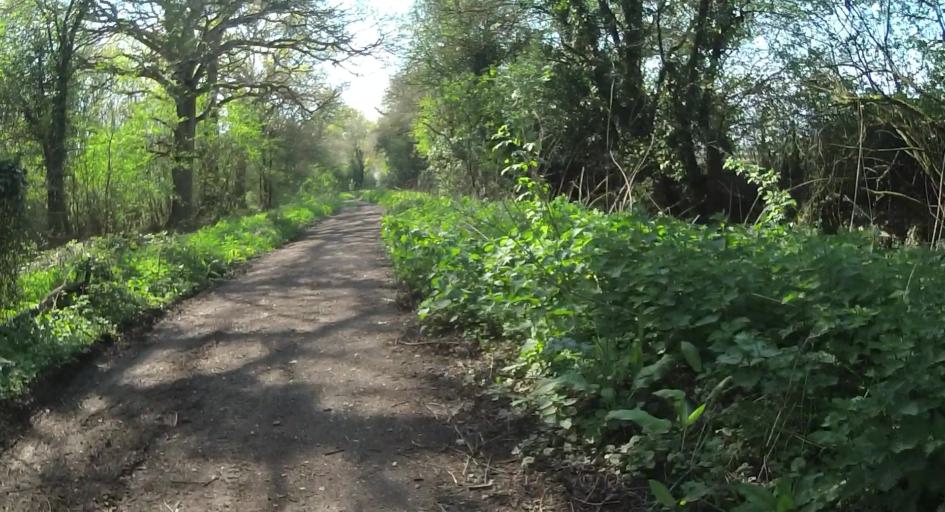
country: GB
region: England
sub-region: West Berkshire
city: Stratfield Mortimer
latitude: 51.3594
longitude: -1.0085
